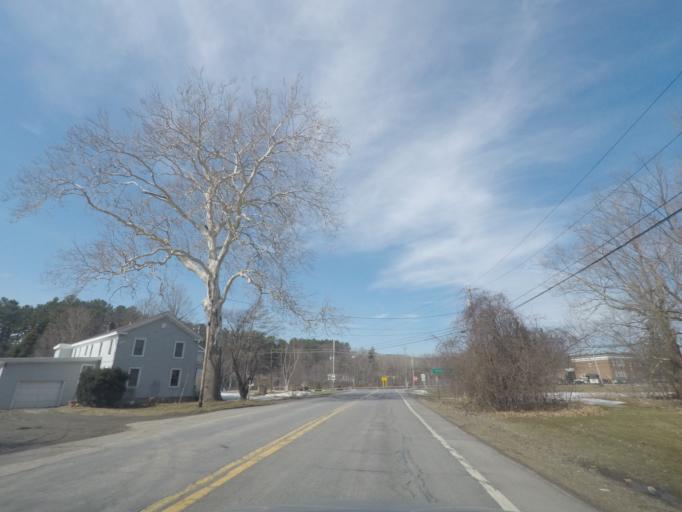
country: US
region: Massachusetts
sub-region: Berkshire County
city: Richmond
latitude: 42.4732
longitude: -73.3810
